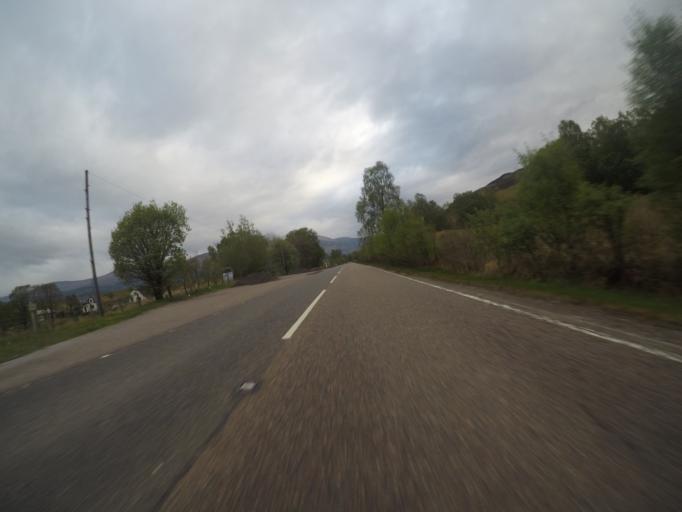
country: GB
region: Scotland
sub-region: Highland
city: Spean Bridge
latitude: 56.9169
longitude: -4.9457
